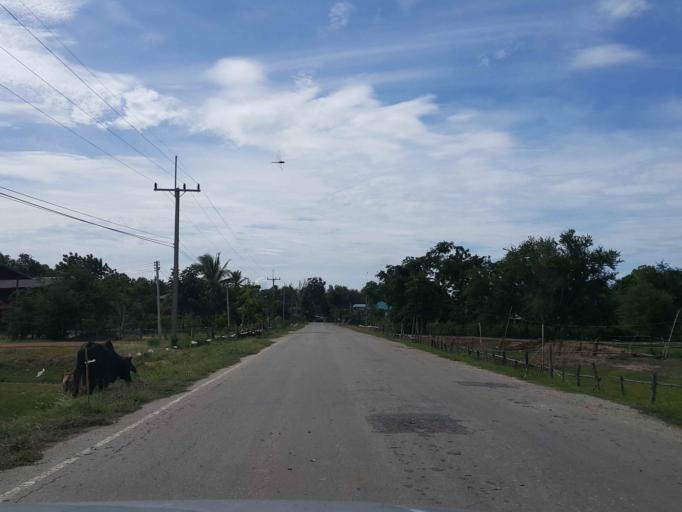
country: TH
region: Sukhothai
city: Ban Dan Lan Hoi
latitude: 17.1192
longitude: 99.5341
